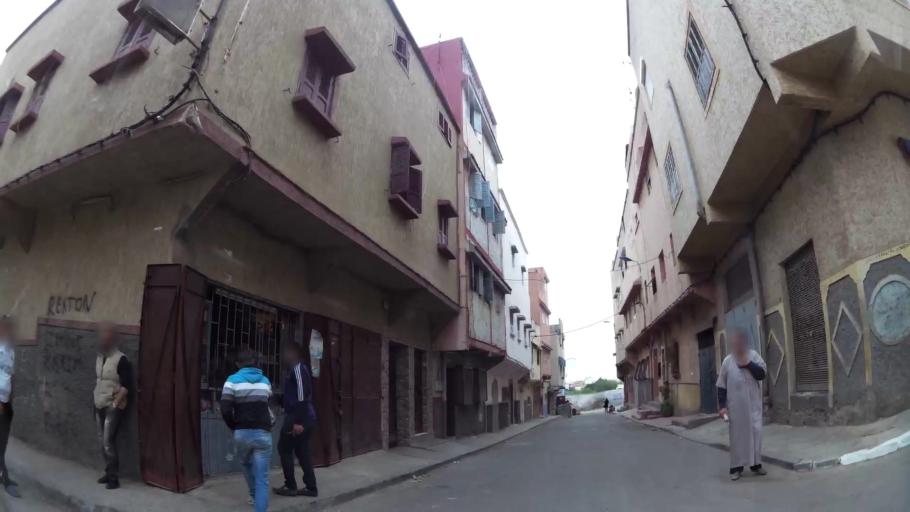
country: MA
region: Rabat-Sale-Zemmour-Zaer
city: Sale
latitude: 34.0363
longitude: -6.8035
